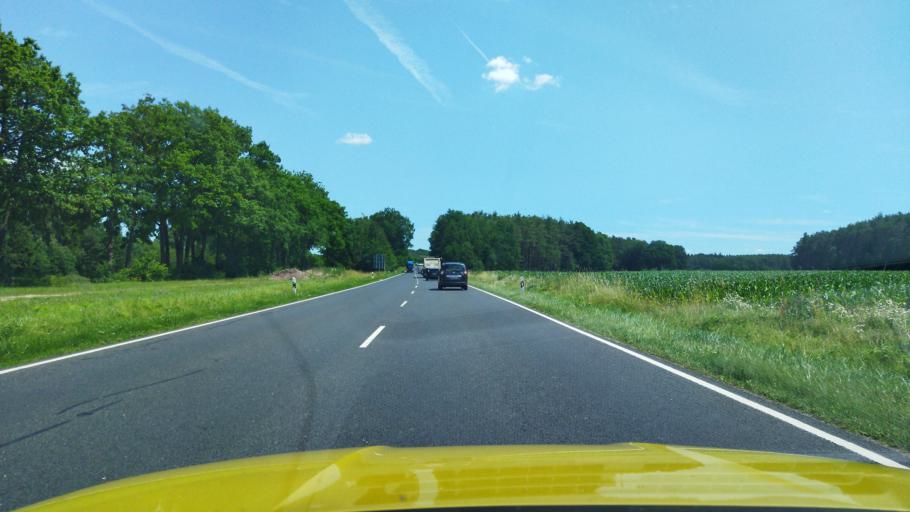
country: DE
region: Bavaria
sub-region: Regierungsbezirk Mittelfranken
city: Allersberg
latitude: 49.2518
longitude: 11.1822
